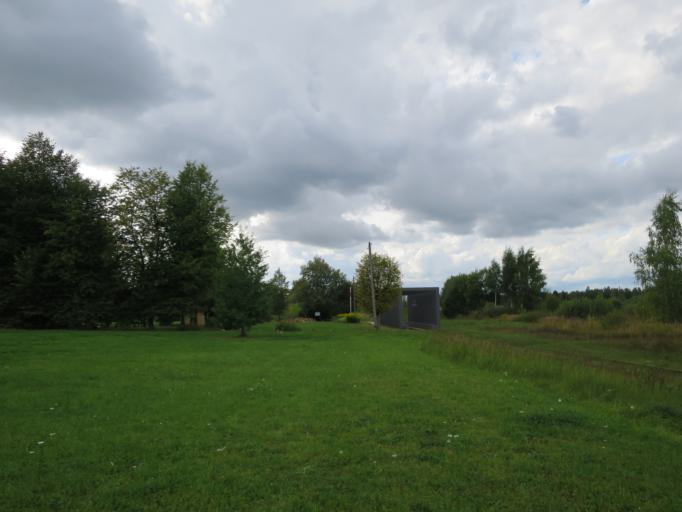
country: LV
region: Malpils
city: Malpils
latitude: 56.8959
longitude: 25.1879
